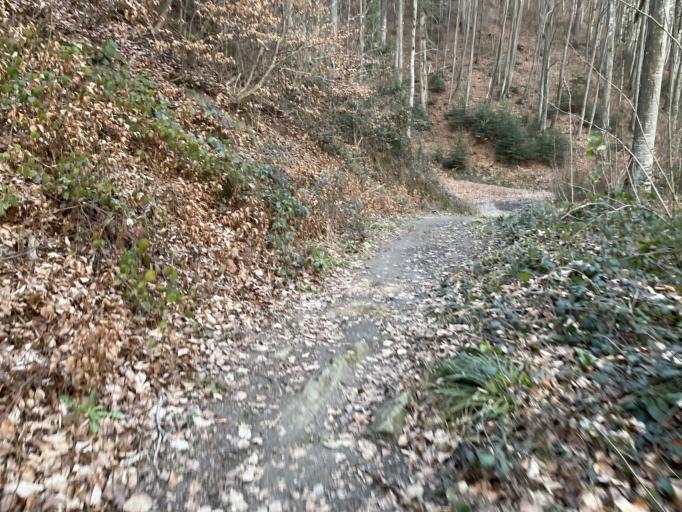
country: CH
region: Bern
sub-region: Bern-Mittelland District
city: Muhlethurnen
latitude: 46.8385
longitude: 7.5288
